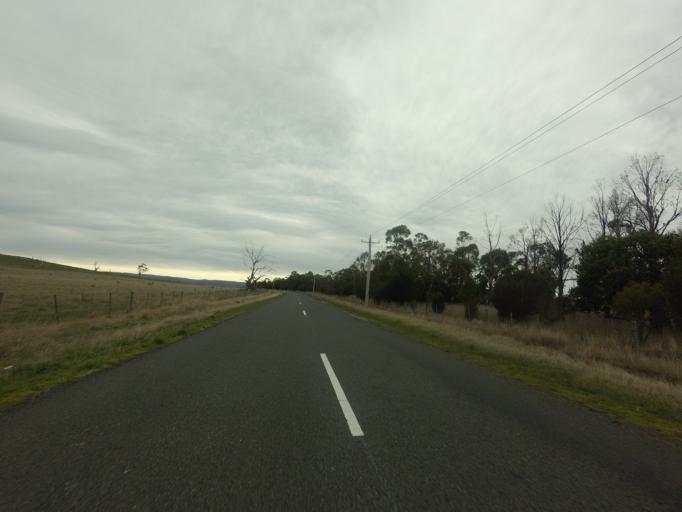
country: AU
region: Tasmania
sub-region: Derwent Valley
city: New Norfolk
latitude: -42.4136
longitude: 147.0065
